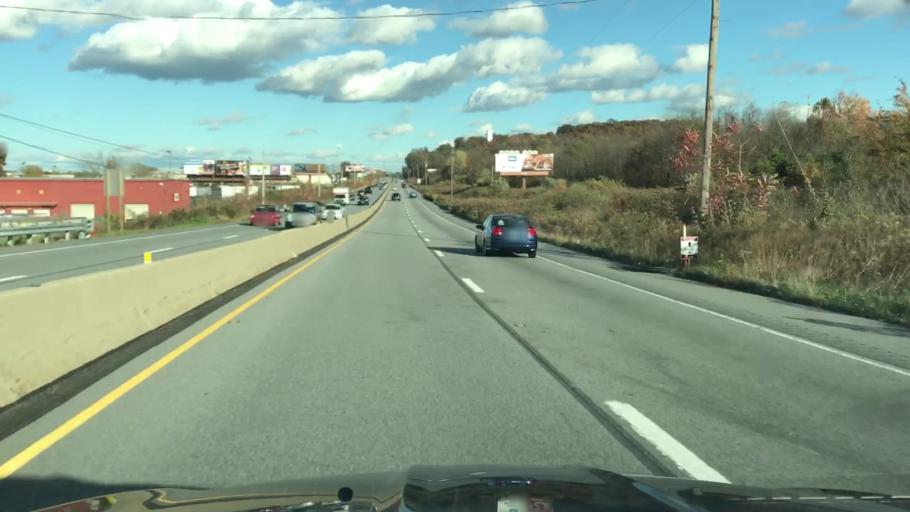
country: US
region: Pennsylvania
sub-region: Dauphin County
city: Lawnton
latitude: 40.2570
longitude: -76.7897
